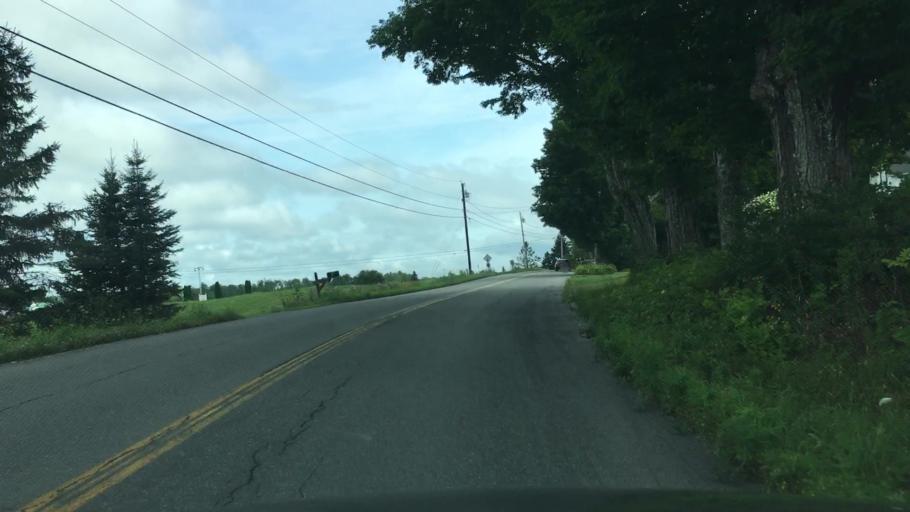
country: US
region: Maine
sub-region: Waldo County
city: Winterport
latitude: 44.6810
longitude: -68.8681
